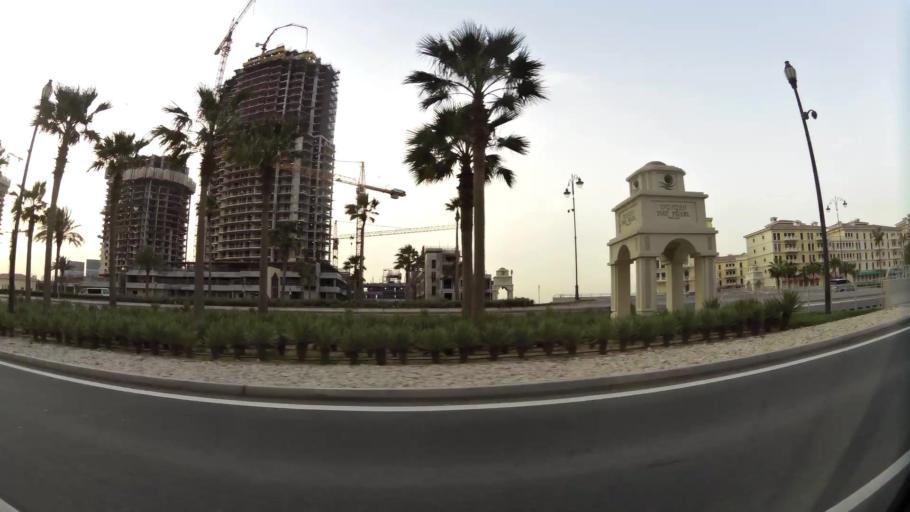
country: QA
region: Baladiyat ad Dawhah
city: Doha
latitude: 25.3738
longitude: 51.5414
